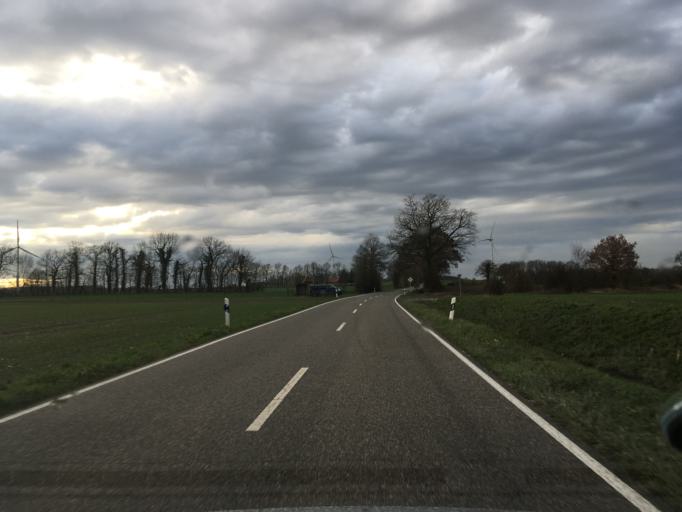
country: DE
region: North Rhine-Westphalia
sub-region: Regierungsbezirk Munster
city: Schoppingen
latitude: 52.0757
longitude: 7.2048
